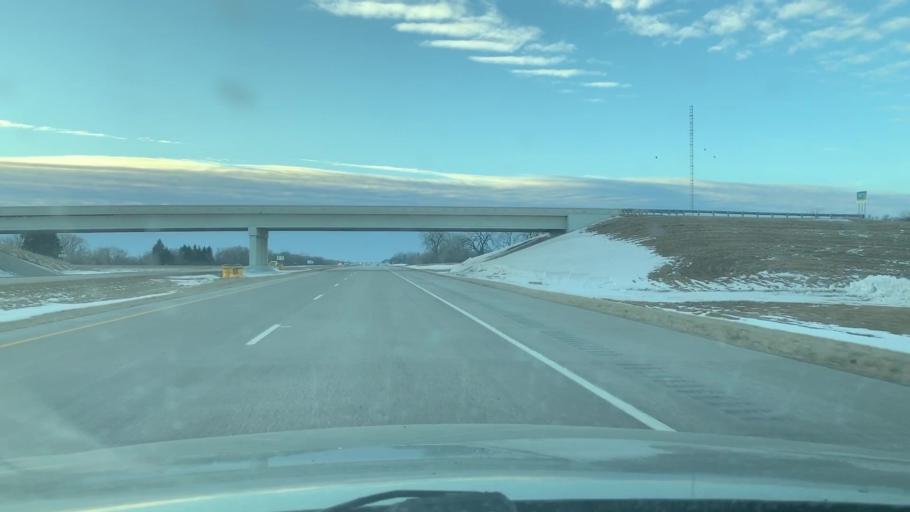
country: US
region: North Dakota
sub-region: Cass County
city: Casselton
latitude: 46.8766
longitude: -97.4293
